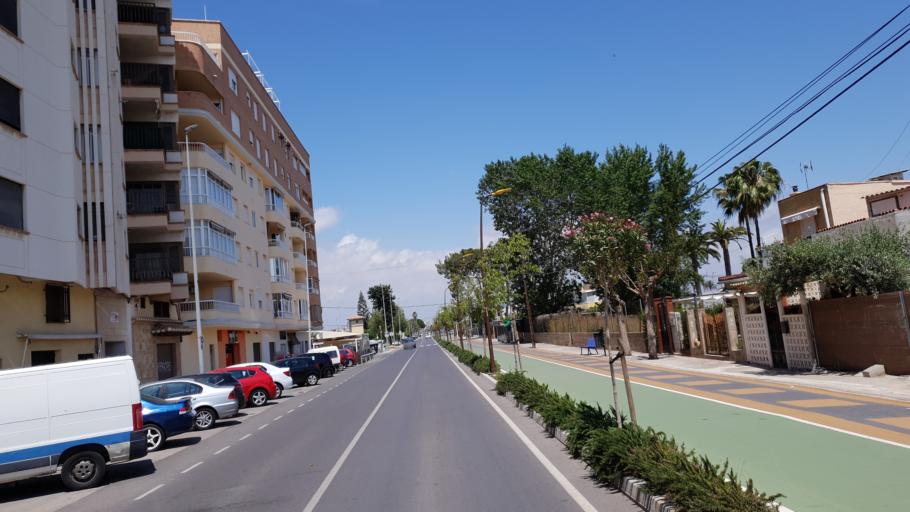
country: ES
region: Valencia
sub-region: Provincia de Castello
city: Burriana
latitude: 39.8665
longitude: -0.0721
